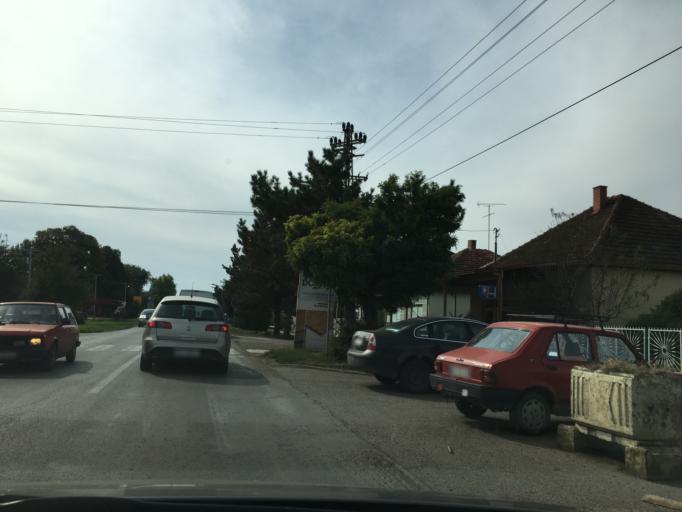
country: RS
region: Autonomna Pokrajina Vojvodina
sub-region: Juznobacki Okrug
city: Temerin
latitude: 45.4281
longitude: 19.8957
